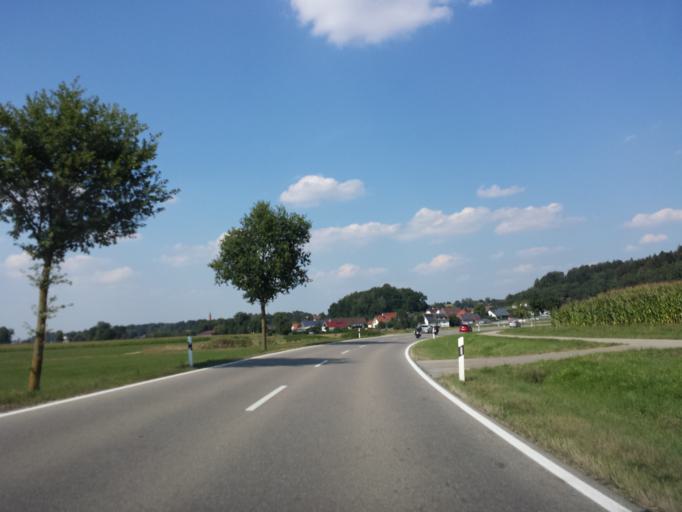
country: DE
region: Bavaria
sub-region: Swabia
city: Ellzee
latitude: 48.3048
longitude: 10.3338
